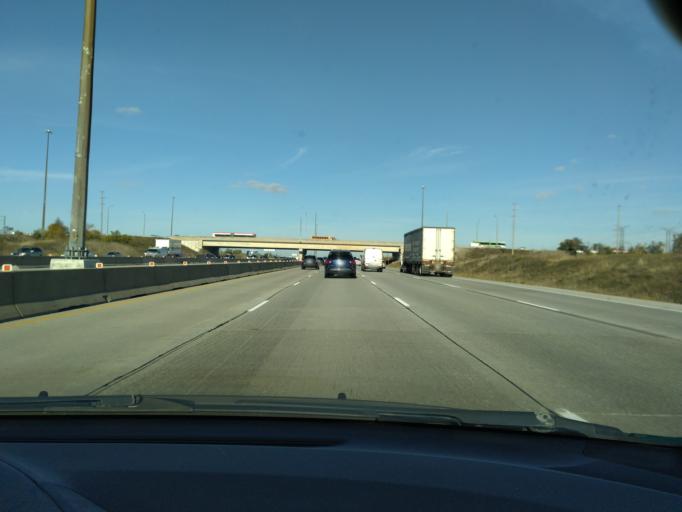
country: CA
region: Ontario
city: Brampton
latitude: 43.6519
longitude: -79.7185
